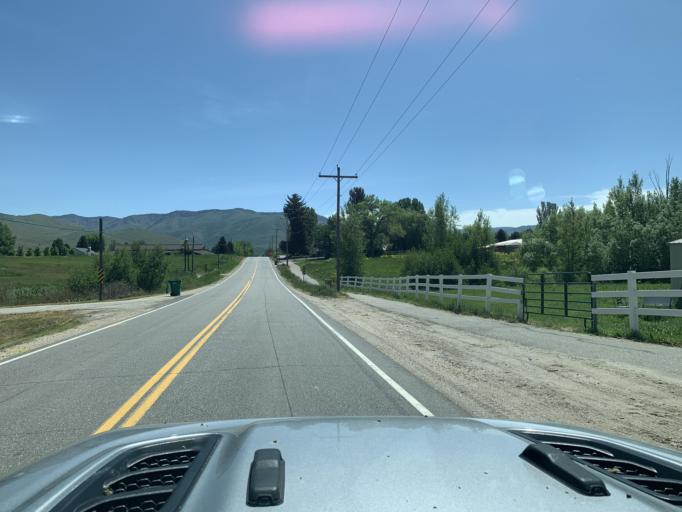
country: US
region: Utah
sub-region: Weber County
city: Wolf Creek
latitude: 41.2933
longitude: -111.7979
